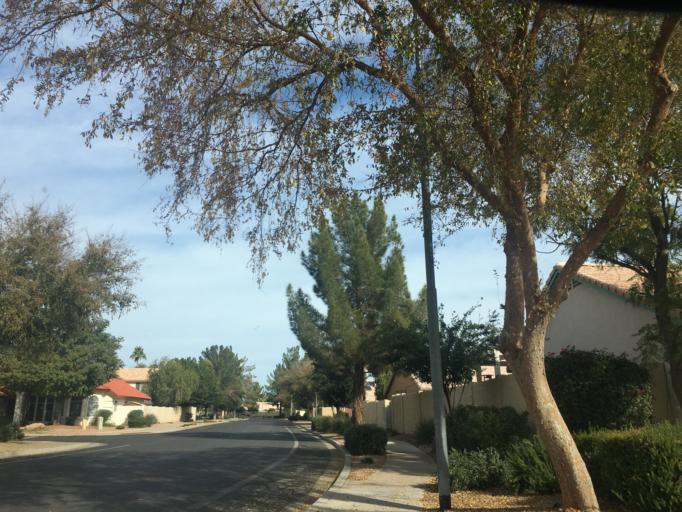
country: US
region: Arizona
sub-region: Maricopa County
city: Gilbert
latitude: 33.3441
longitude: -111.8040
